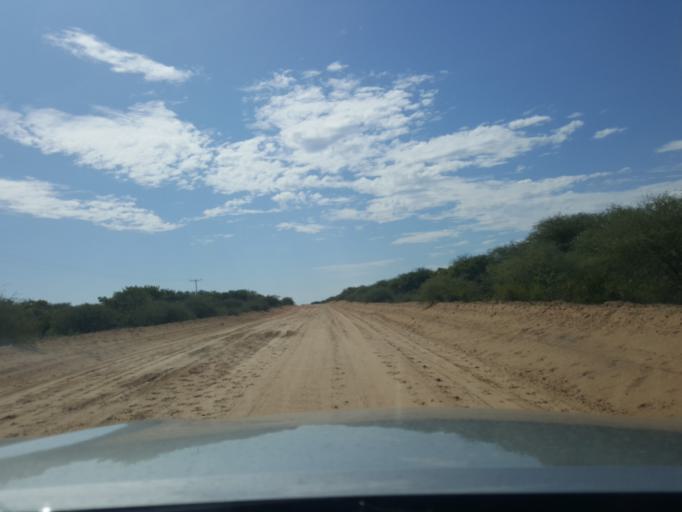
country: BW
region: Kweneng
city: Khudumelapye
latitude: -23.8713
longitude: 24.8973
